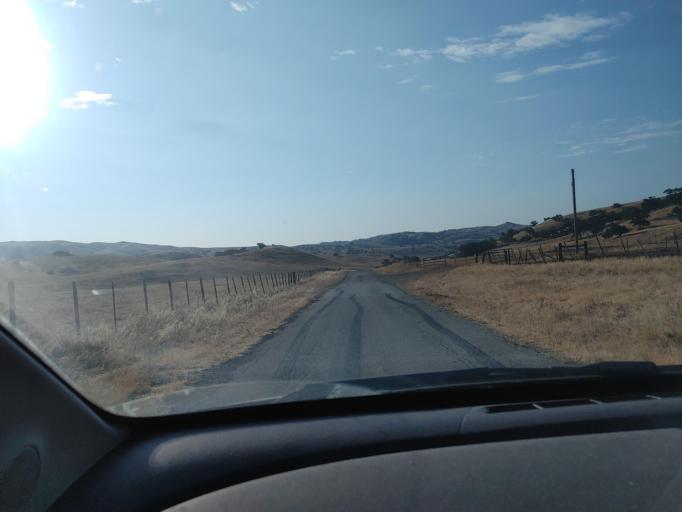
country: US
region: California
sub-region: San Benito County
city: Ridgemark
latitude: 36.7626
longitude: -121.1756
